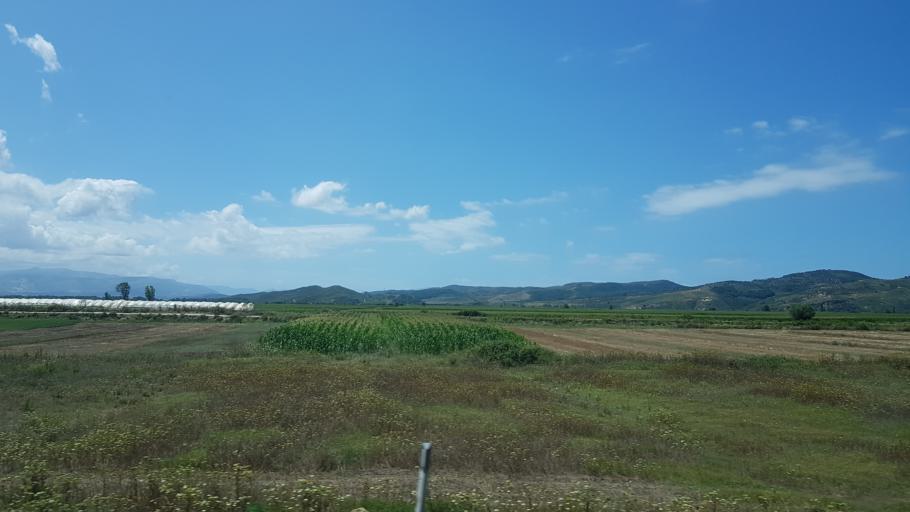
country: AL
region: Fier
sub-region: Rrethi i Fierit
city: Cakran
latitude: 40.6004
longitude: 19.5617
